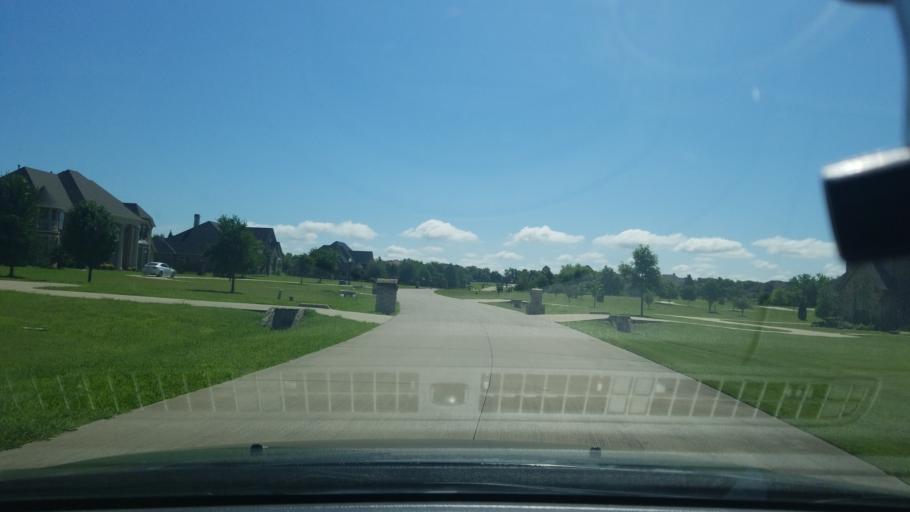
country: US
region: Texas
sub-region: Dallas County
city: Sunnyvale
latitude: 32.7983
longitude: -96.5700
